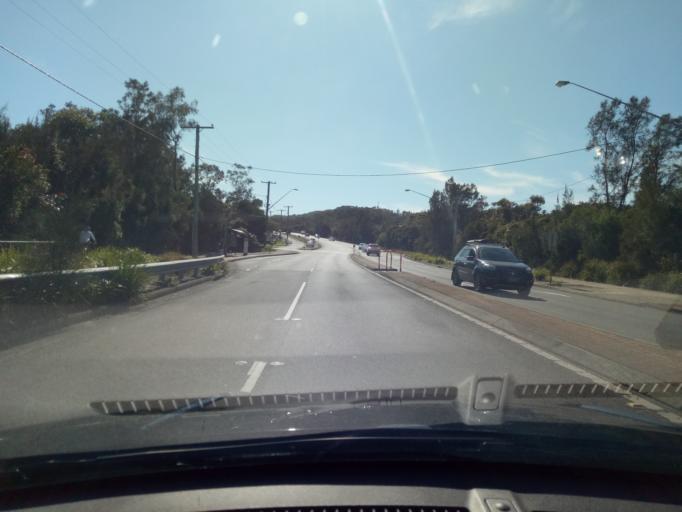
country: AU
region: New South Wales
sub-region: Gosford Shire
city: Forresters Beach
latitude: -33.4102
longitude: 151.4595
